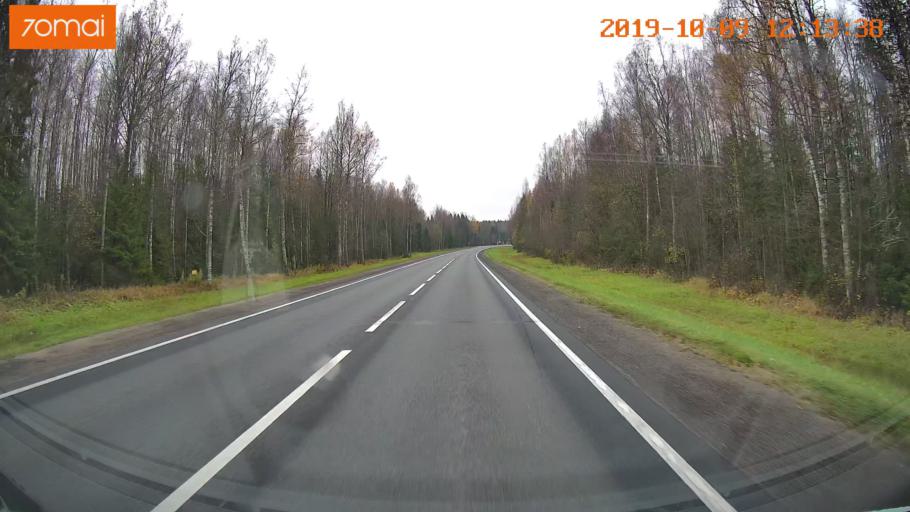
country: RU
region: Jaroslavl
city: Prechistoye
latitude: 58.5074
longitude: 40.3447
